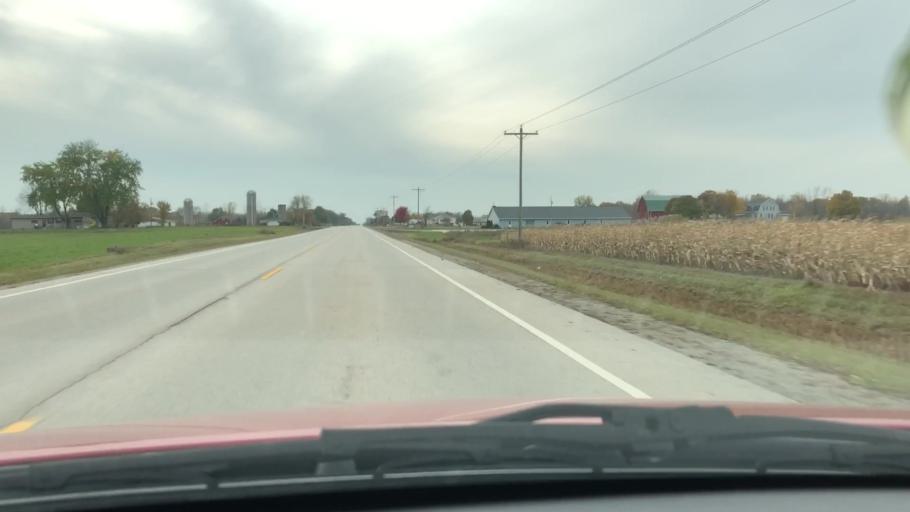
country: US
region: Wisconsin
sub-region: Brown County
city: Oneida
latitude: 44.4443
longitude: -88.1672
